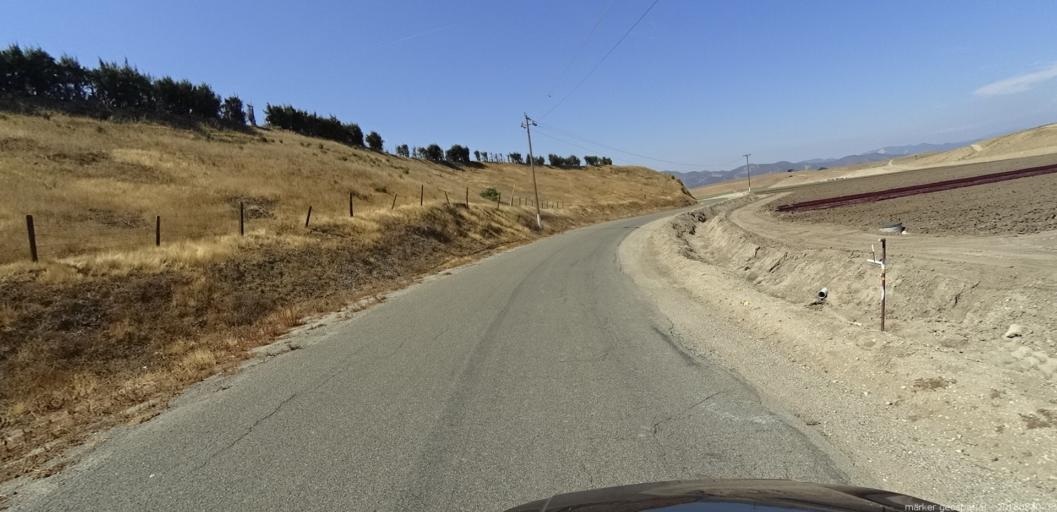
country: US
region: California
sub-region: Monterey County
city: King City
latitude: 36.1112
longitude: -121.0397
